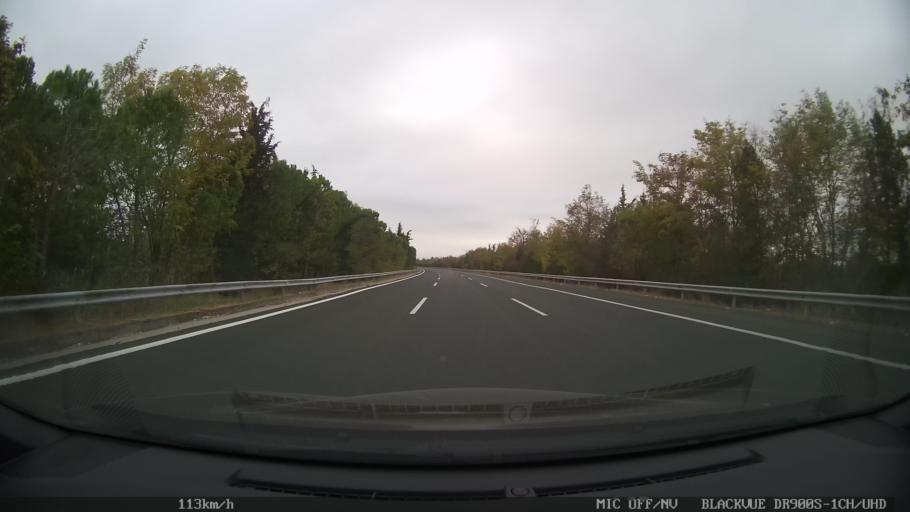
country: GR
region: Central Macedonia
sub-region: Nomos Pierias
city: Aiginio
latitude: 40.4937
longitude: 22.5642
